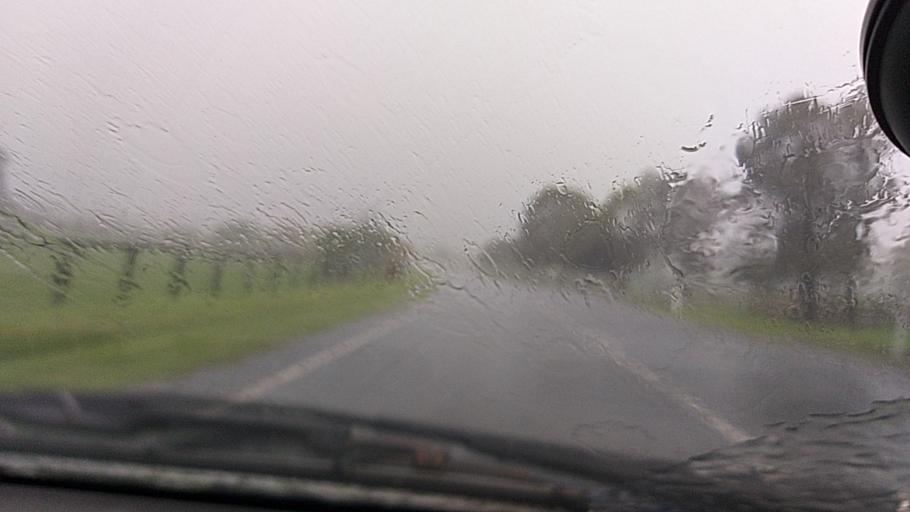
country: AU
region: New South Wales
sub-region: Wollondilly
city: Douglas Park
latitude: -34.1385
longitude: 150.7130
